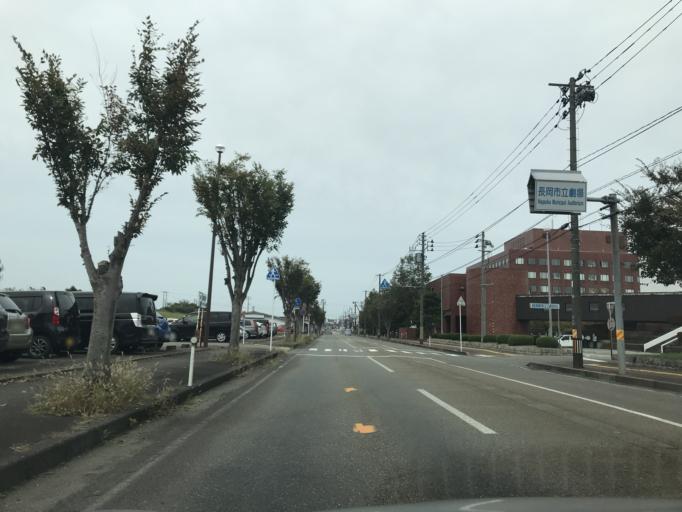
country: JP
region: Niigata
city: Nagaoka
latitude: 37.4350
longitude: 138.8378
